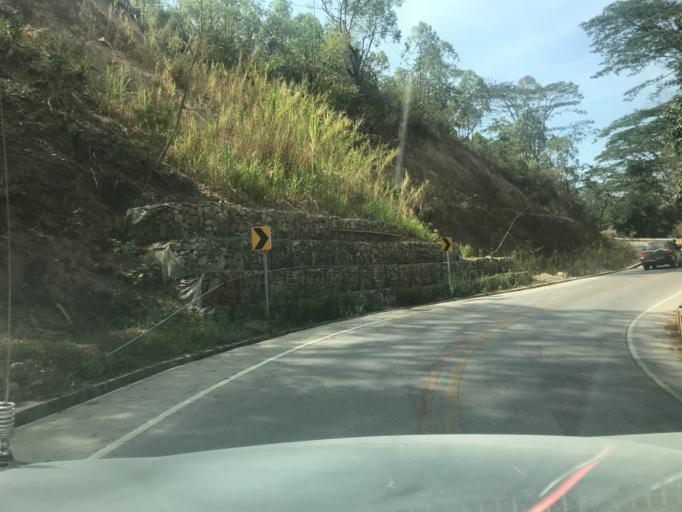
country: TL
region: Aileu
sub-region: Aileu Villa
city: Aileu
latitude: -8.6789
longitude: 125.5513
